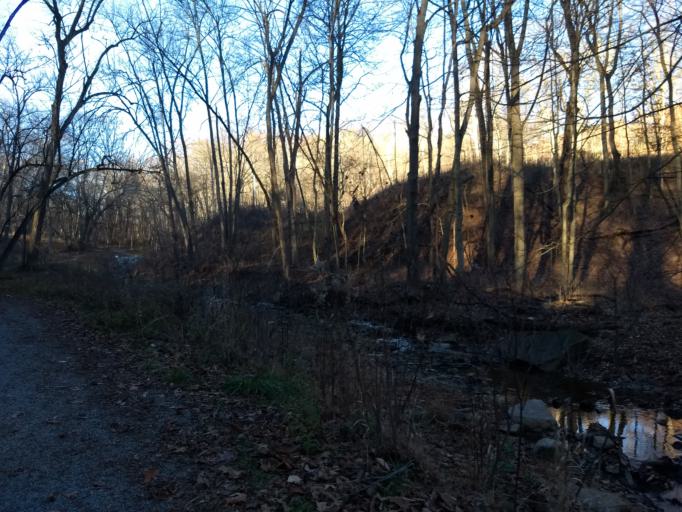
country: US
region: Pennsylvania
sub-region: Allegheny County
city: South Park Township
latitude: 40.2902
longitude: -80.0023
